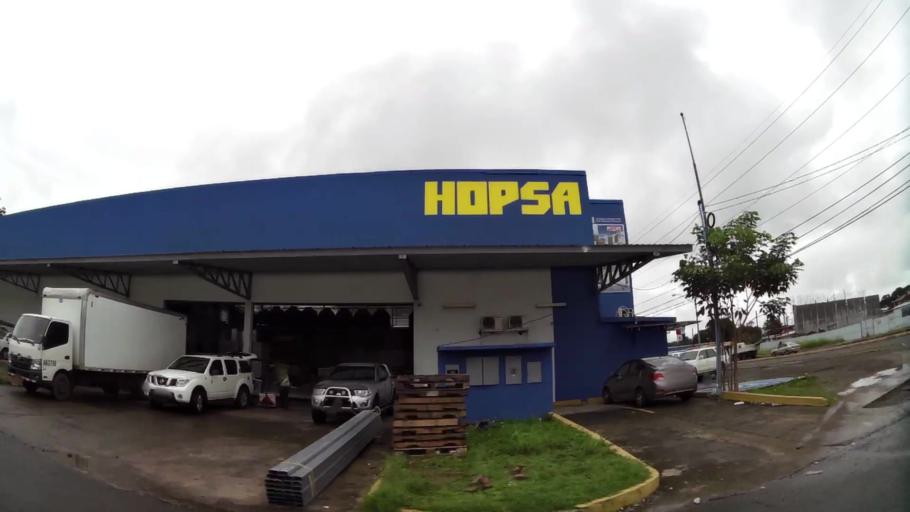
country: PA
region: Chiriqui
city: David
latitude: 8.4343
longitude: -82.4405
